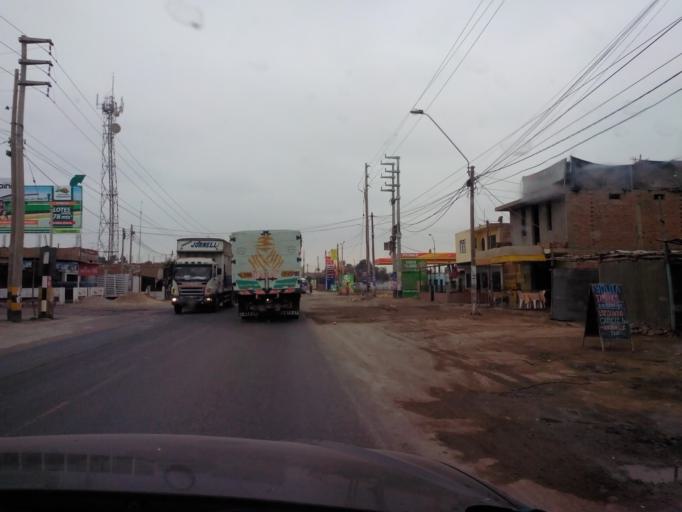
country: PE
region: Ica
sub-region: Provincia de Chincha
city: Chincha Baja
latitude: -13.4475
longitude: -76.1358
